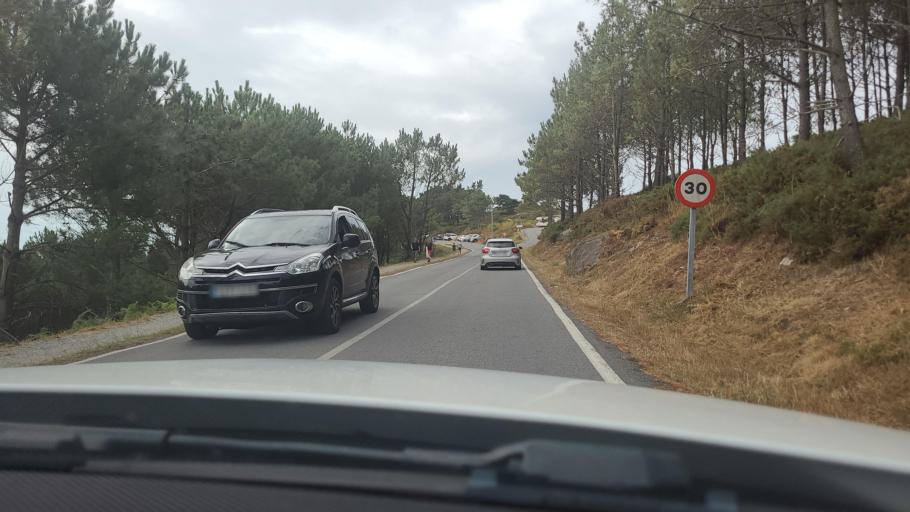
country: ES
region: Galicia
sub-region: Provincia da Coruna
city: Fisterra
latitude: 42.8876
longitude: -9.2709
